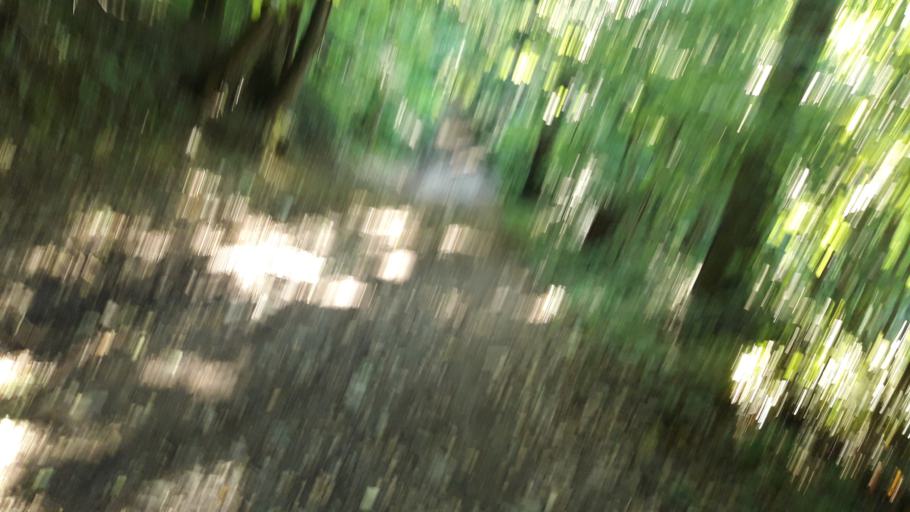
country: FR
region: Rhone-Alpes
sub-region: Departement de l'Isere
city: Saint-Martin-d'Heres
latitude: 45.1585
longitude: 5.7792
